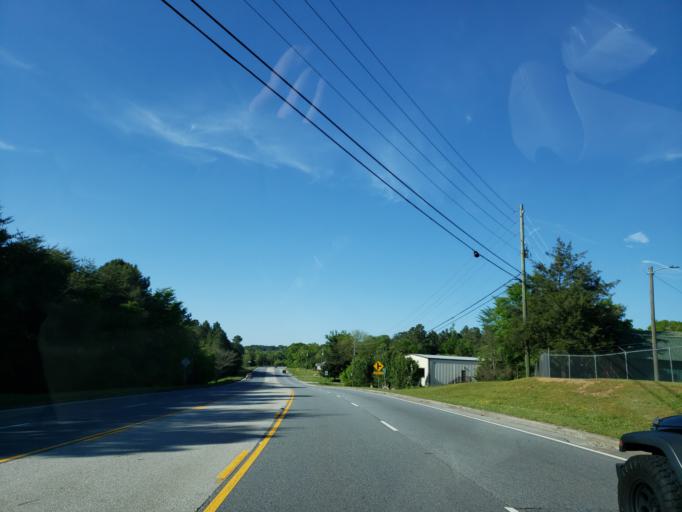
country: US
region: Georgia
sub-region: Polk County
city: Cedartown
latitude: 33.9741
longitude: -85.2582
